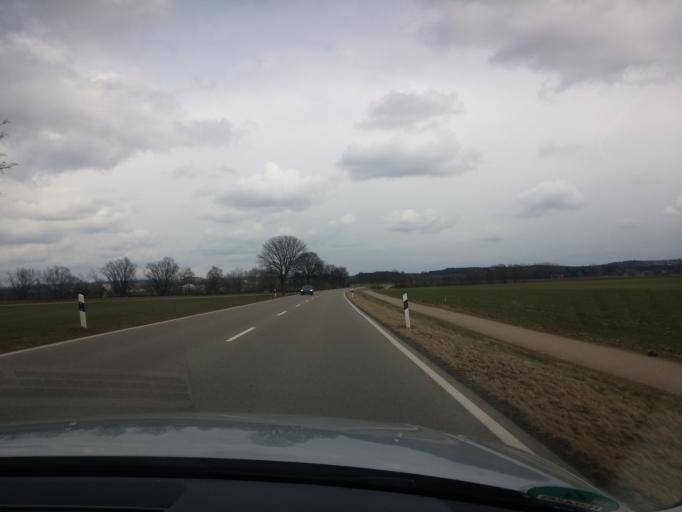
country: DE
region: Bavaria
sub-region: Swabia
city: Lachen
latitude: 47.9627
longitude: 10.2379
